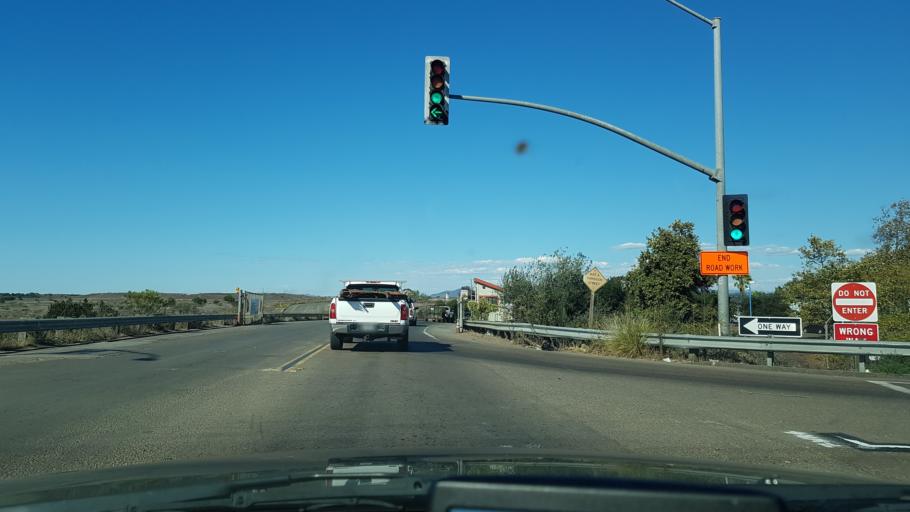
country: US
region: California
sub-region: San Diego County
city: La Jolla
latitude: 32.8384
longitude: -117.1520
